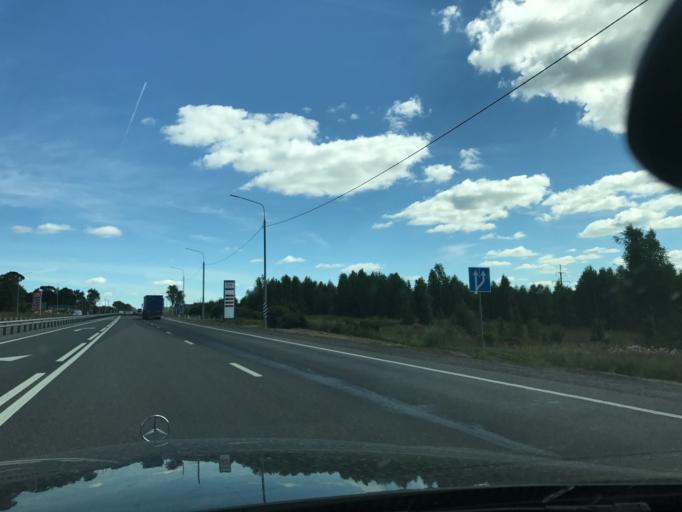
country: RU
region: Vladimir
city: Gorokhovets
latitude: 56.1669
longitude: 42.4660
